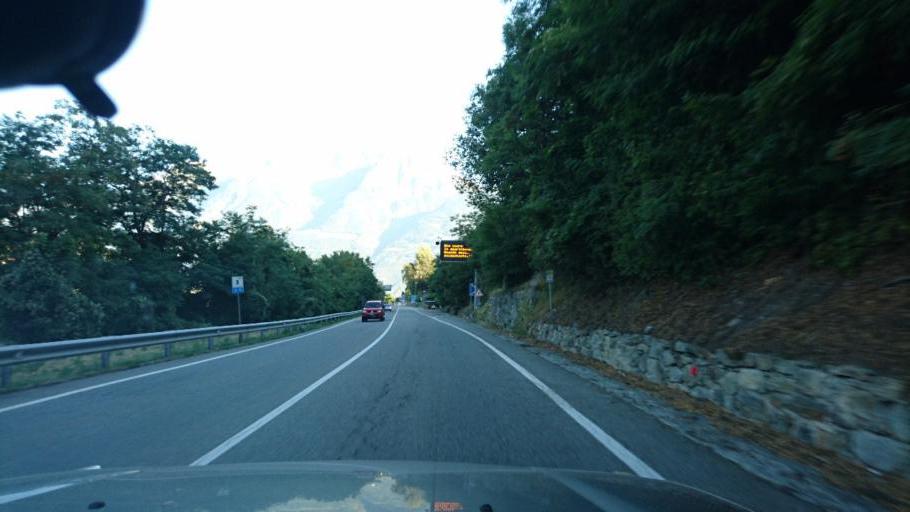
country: IT
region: Aosta Valley
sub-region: Valle d'Aosta
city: La Cretaz-Roisan
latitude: 45.7710
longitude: 7.3085
